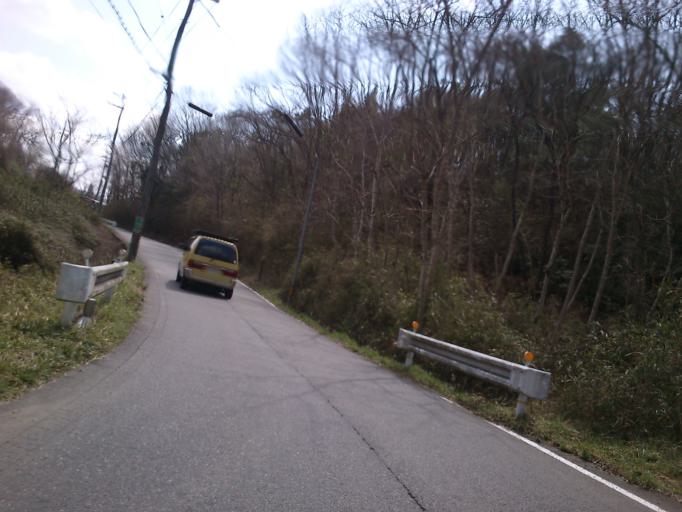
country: JP
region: Mie
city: Ueno-ebisumachi
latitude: 34.7543
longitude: 136.0247
